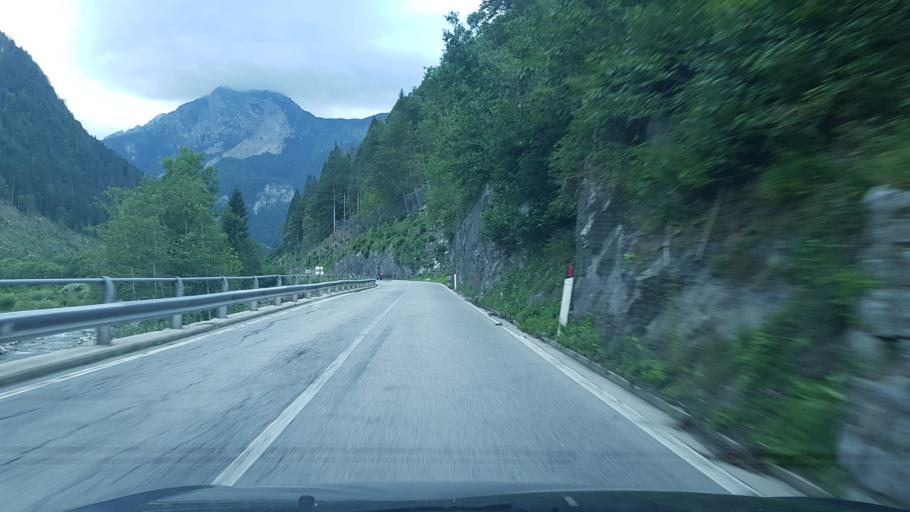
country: IT
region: Friuli Venezia Giulia
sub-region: Provincia di Udine
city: Forni Avoltri
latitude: 46.5737
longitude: 12.7996
